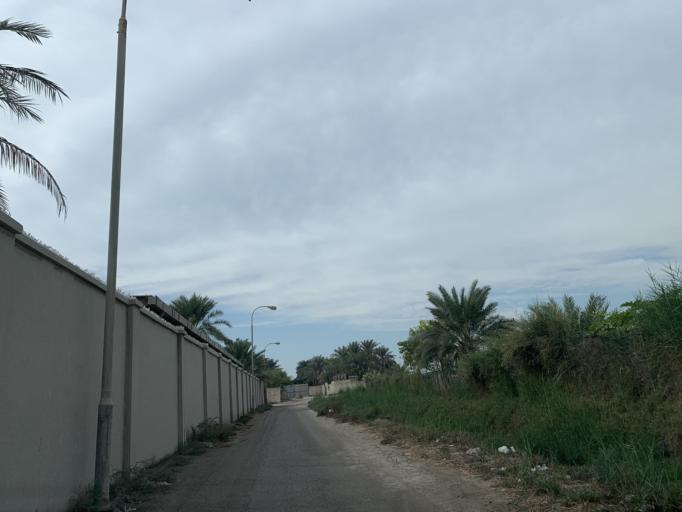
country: BH
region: Central Governorate
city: Madinat Hamad
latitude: 26.1117
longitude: 50.4714
